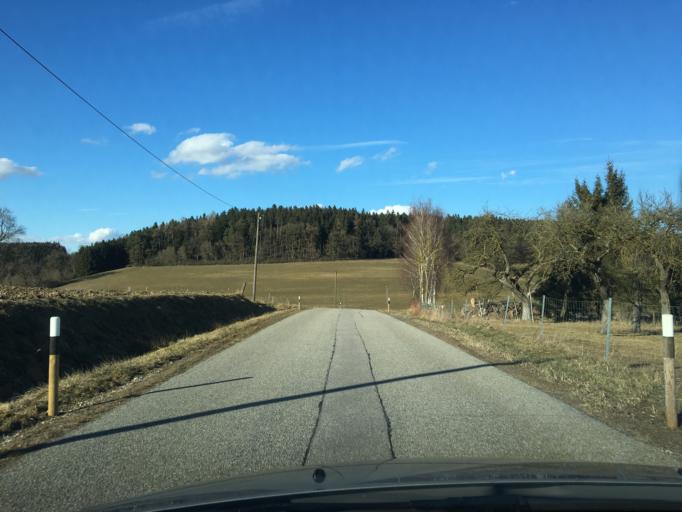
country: DE
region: Bavaria
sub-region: Lower Bavaria
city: Tiefenbach
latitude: 48.4801
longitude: 12.1143
